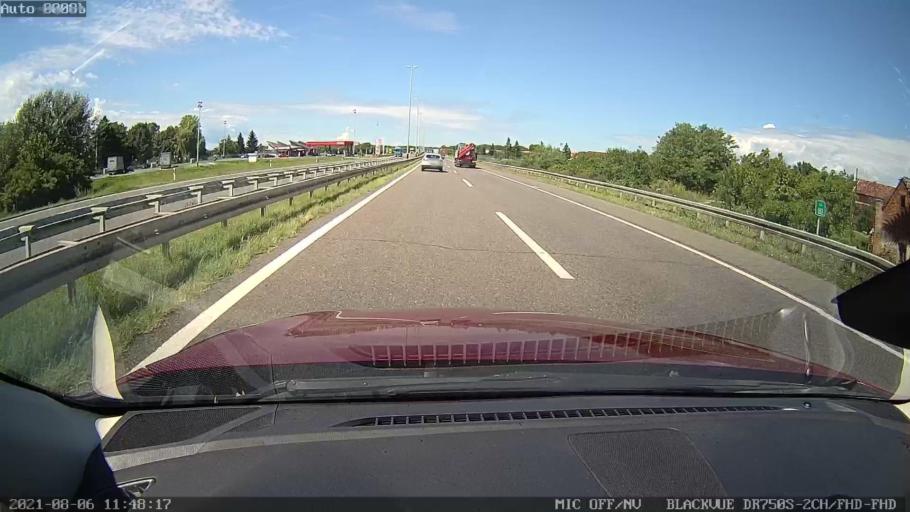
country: HR
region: Brodsko-Posavska
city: Luzani
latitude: 45.1629
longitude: 17.7040
